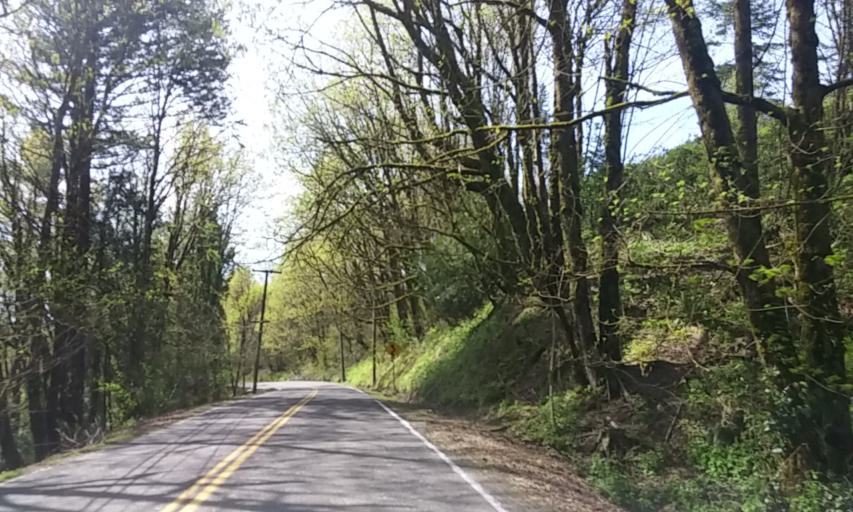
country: US
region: Oregon
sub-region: Washington County
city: West Haven-Sylvan
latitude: 45.5248
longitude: -122.7467
